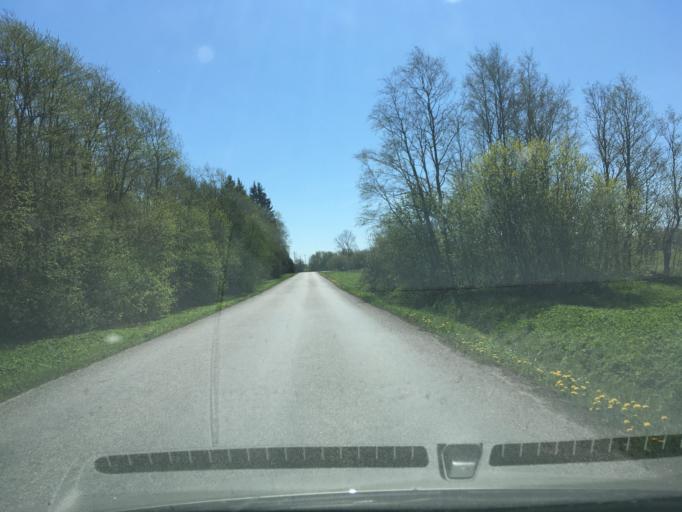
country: EE
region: Harju
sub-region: Raasiku vald
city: Arukula
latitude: 59.4080
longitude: 25.0773
